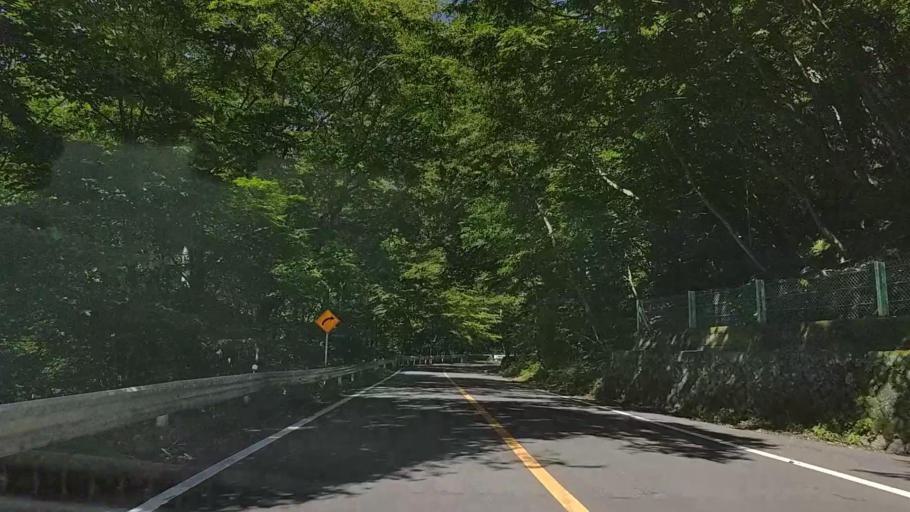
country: JP
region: Nagano
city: Saku
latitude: 36.3535
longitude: 138.6646
